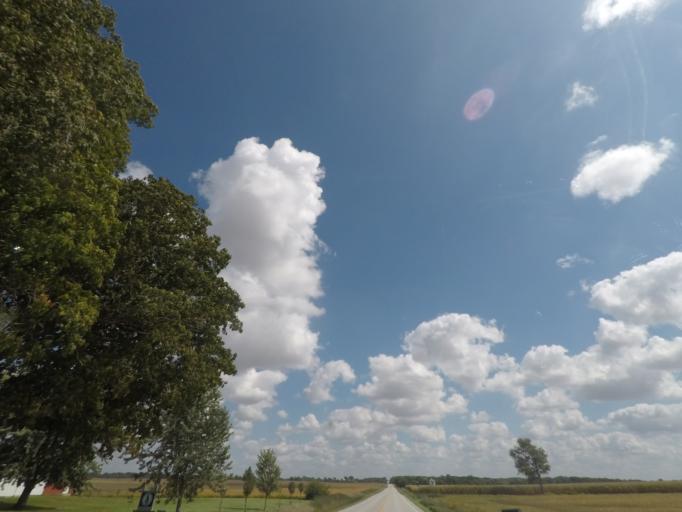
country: US
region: Iowa
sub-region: Story County
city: Nevada
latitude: 42.0779
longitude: -93.3740
